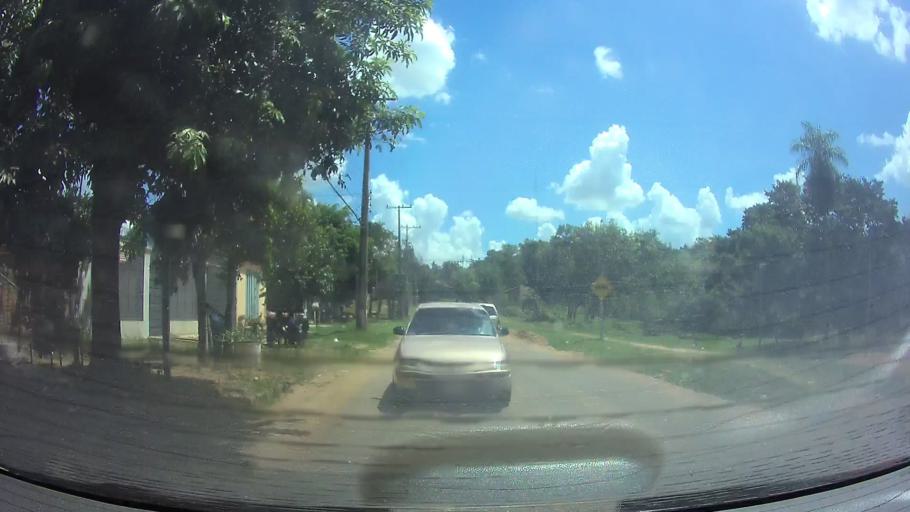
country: PY
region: Central
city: Limpio
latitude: -25.1674
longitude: -57.4441
